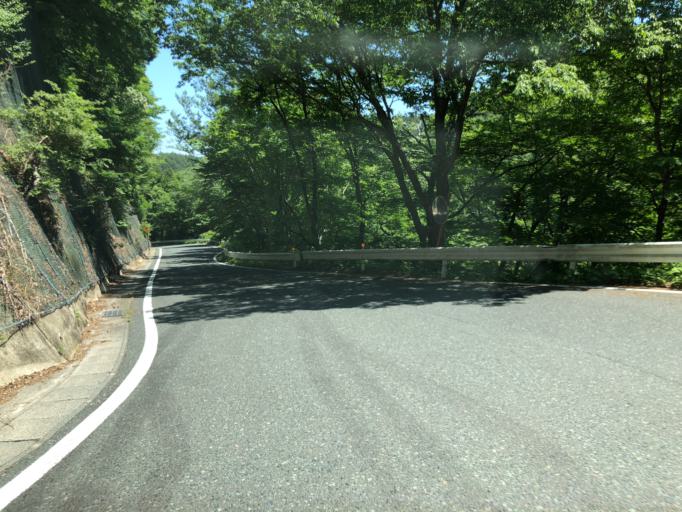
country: JP
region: Fukushima
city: Namie
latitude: 37.5134
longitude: 140.8460
